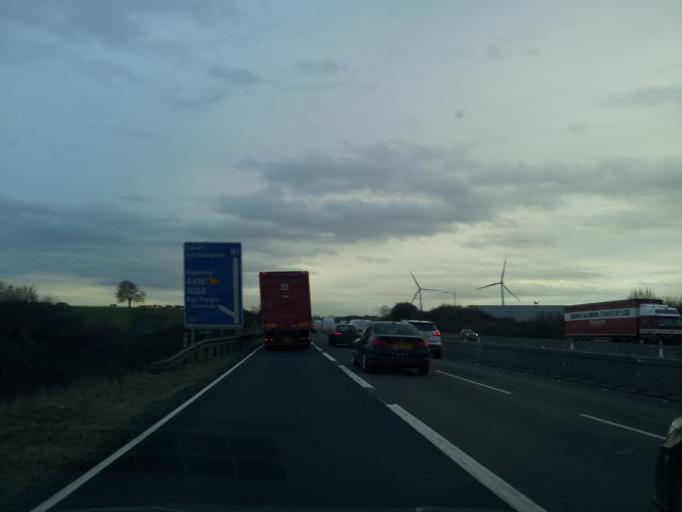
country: GB
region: England
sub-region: Northamptonshire
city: Long Buckby
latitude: 52.3572
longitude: -1.1557
